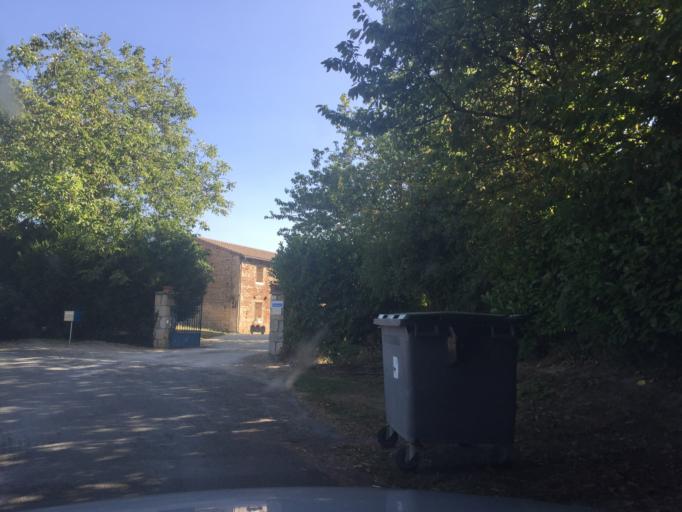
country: FR
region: Poitou-Charentes
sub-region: Departement des Deux-Sevres
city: Lezay
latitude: 46.1999
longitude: -0.0367
